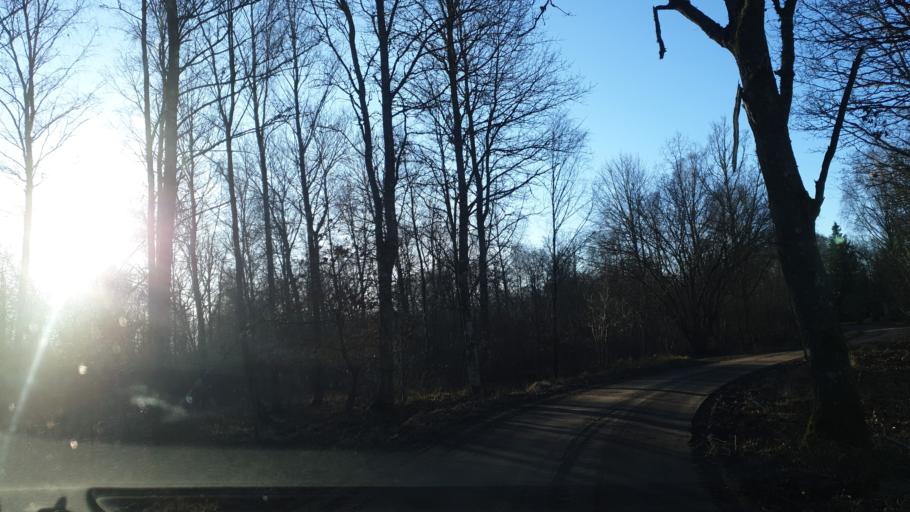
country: SE
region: Blekinge
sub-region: Karlskrona Kommun
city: Nattraby
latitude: 56.2546
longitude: 15.4087
